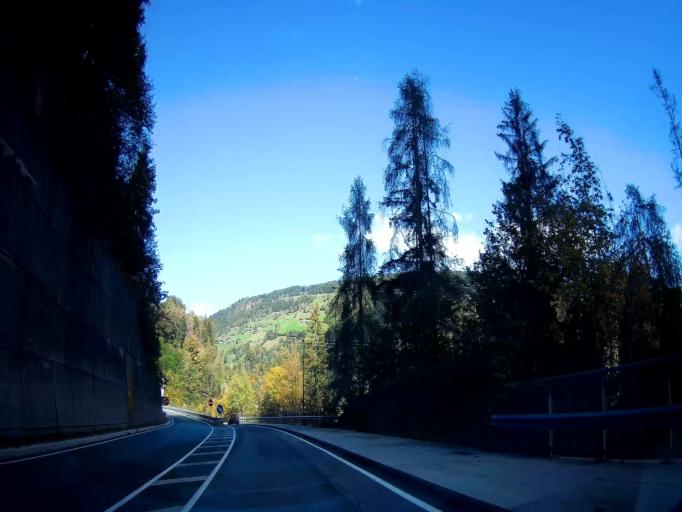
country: AT
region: Salzburg
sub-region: Politischer Bezirk Zell am See
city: Lend
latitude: 47.2841
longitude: 13.0698
